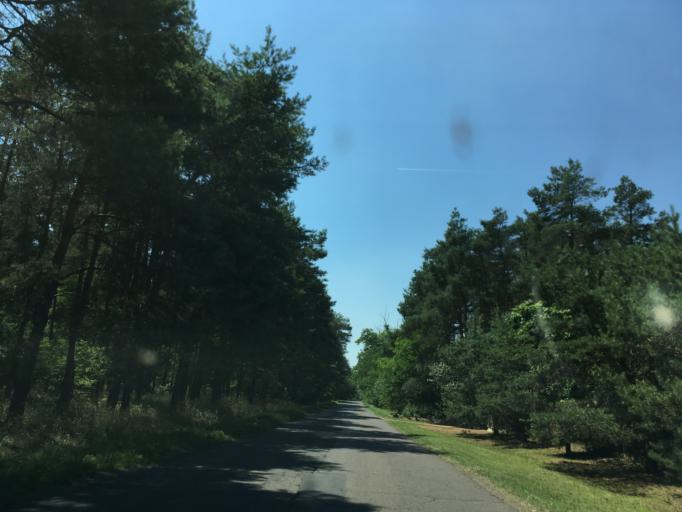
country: HU
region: Hajdu-Bihar
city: Mikepercs
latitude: 47.4766
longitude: 21.7070
